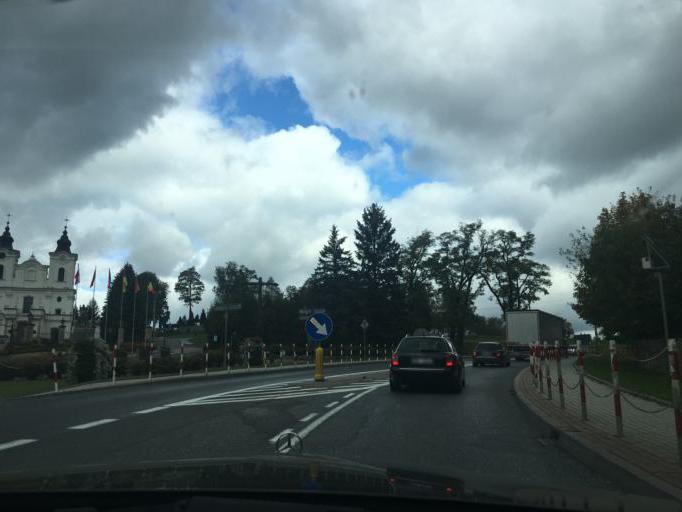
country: PL
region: Subcarpathian Voivodeship
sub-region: Powiat krosnienski
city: Dukla
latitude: 49.5580
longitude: 21.6829
